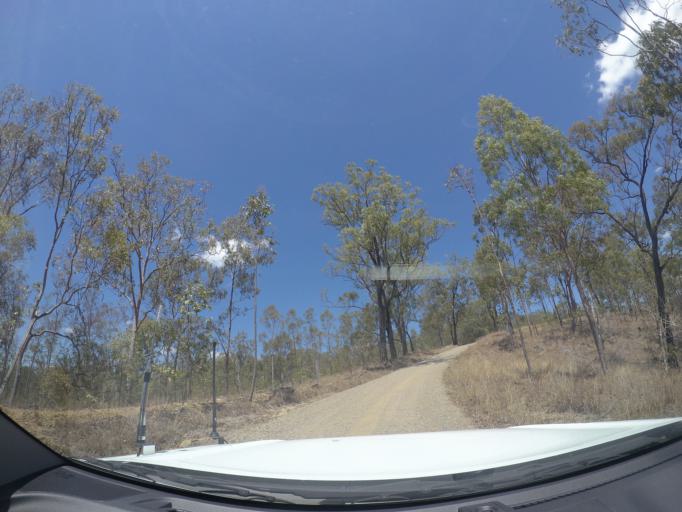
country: AU
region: Queensland
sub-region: Ipswich
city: Springfield Lakes
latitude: -27.8264
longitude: 152.8369
